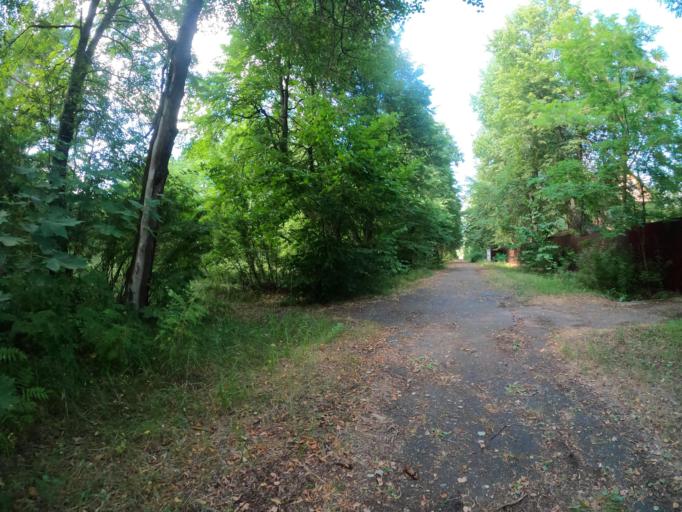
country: RU
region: Moskovskaya
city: Konobeyevo
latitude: 55.3903
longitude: 38.7100
